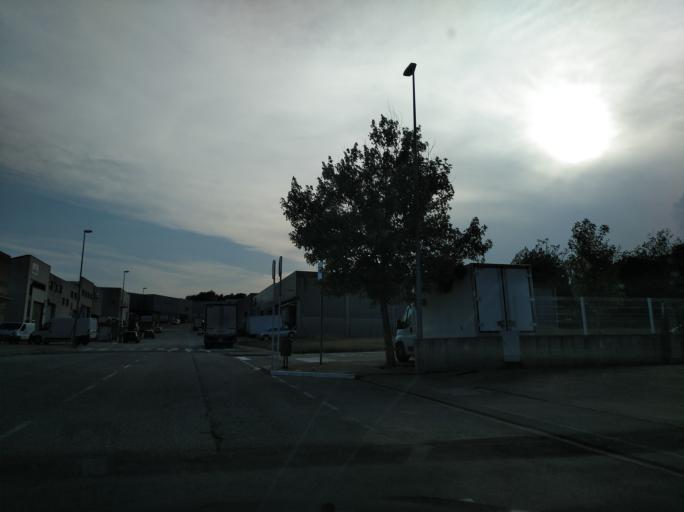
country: ES
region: Catalonia
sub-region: Provincia de Girona
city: Vilablareix
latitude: 41.9425
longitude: 2.7798
